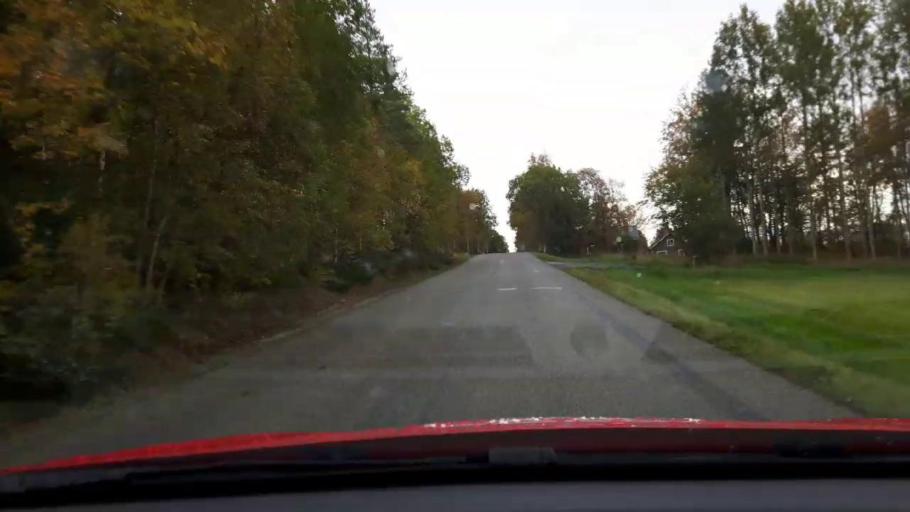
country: SE
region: Jaemtland
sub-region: Bergs Kommun
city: Hoverberg
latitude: 62.9540
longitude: 14.4906
